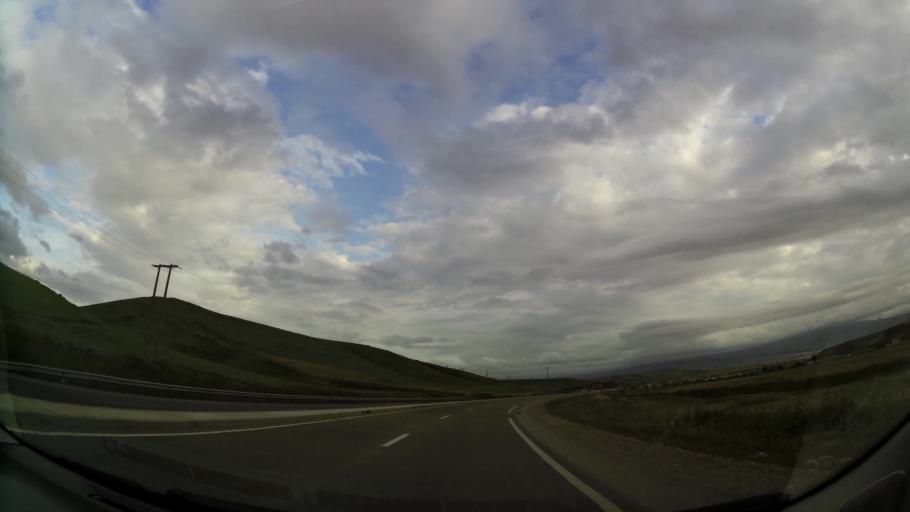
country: MA
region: Taza-Al Hoceima-Taounate
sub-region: Taza
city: Taza
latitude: 34.2782
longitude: -3.9562
